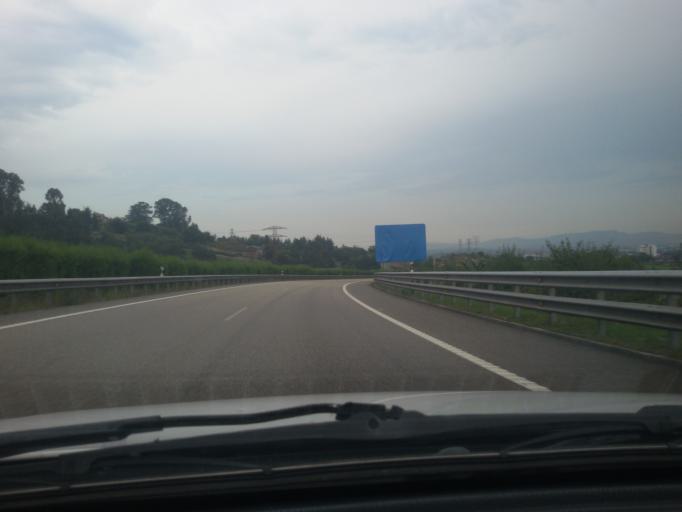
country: ES
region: Asturias
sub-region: Province of Asturias
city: Oviedo
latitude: 43.3788
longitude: -5.8398
